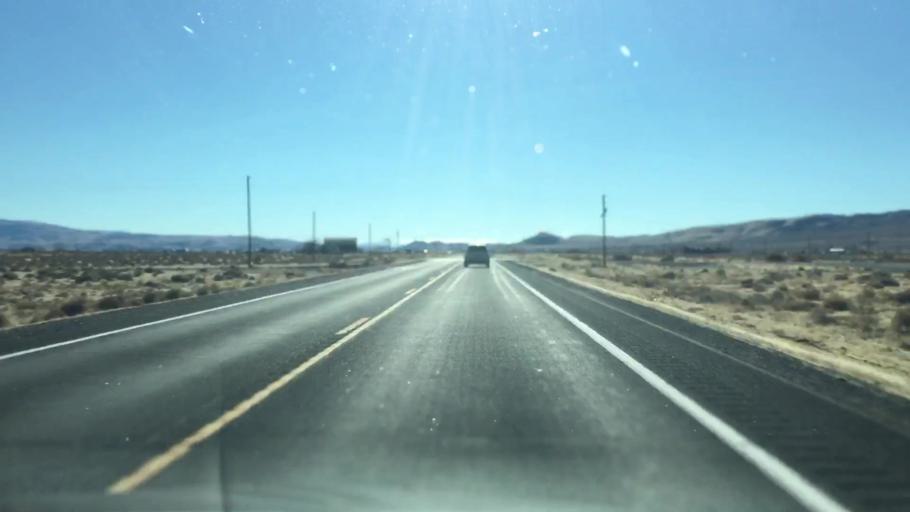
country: US
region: Nevada
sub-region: Lyon County
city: Silver Springs
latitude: 39.3910
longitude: -119.2303
